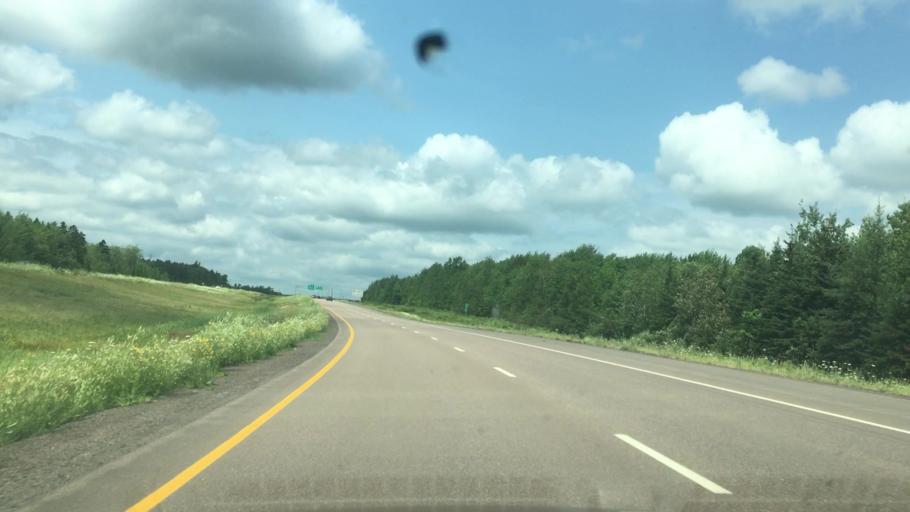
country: CA
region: New Brunswick
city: Dieppe
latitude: 46.0938
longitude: -64.5982
